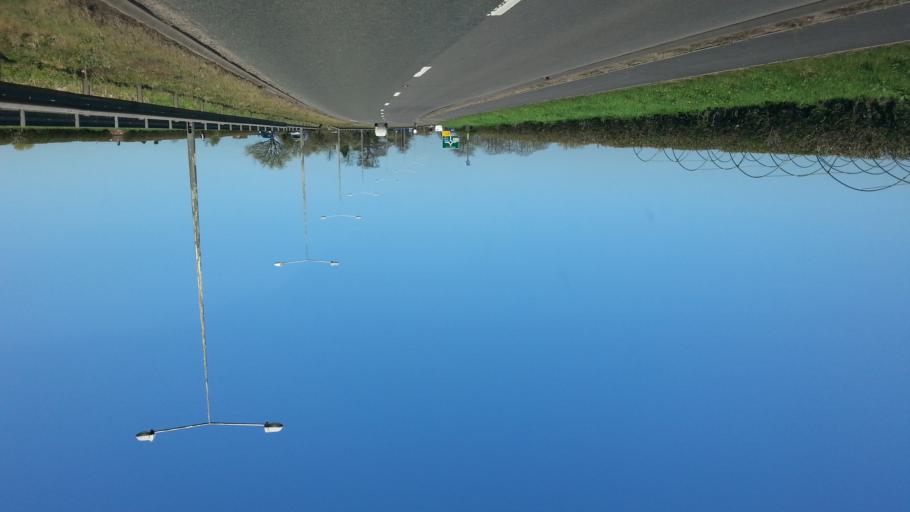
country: GB
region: England
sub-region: Staffordshire
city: Penkridge
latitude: 52.6898
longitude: -2.1320
